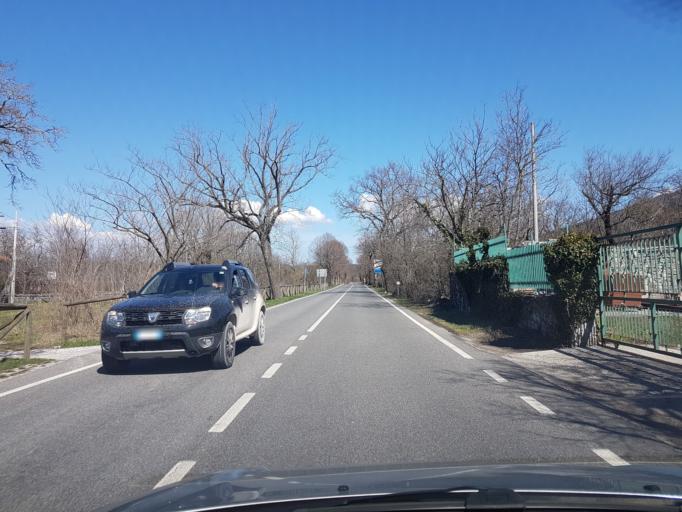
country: IT
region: Friuli Venezia Giulia
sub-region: Provincia di Trieste
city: Dolina
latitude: 45.6439
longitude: 13.8685
